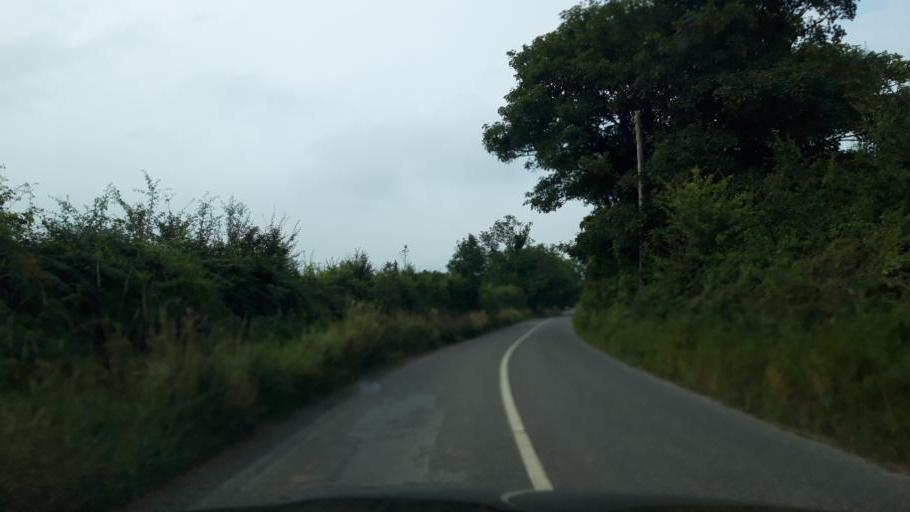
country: IE
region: Munster
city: Fethard
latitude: 52.5838
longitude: -7.5987
